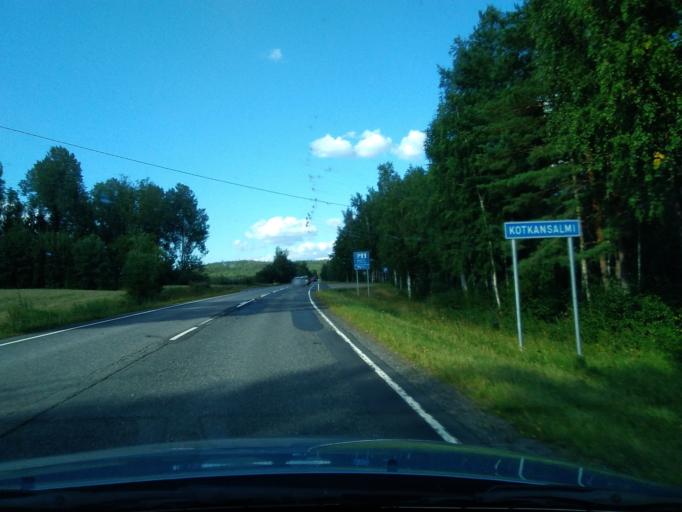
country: FI
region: Pirkanmaa
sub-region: Ylae-Pirkanmaa
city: Maenttae
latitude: 61.9946
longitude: 24.6368
